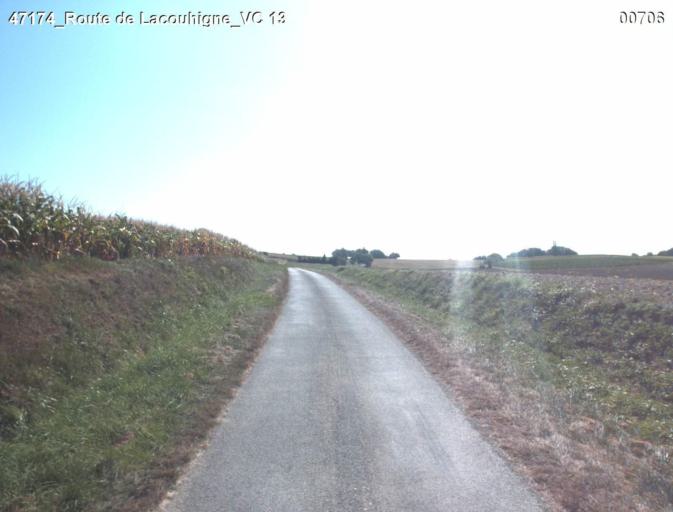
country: FR
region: Midi-Pyrenees
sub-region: Departement du Gers
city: Condom
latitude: 44.0203
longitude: 0.3843
